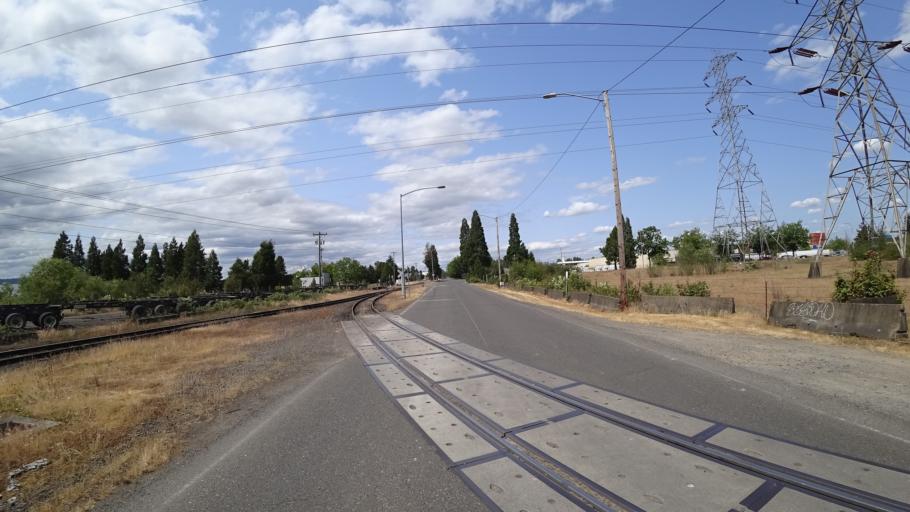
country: US
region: Oregon
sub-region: Washington County
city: Oak Hills
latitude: 45.6182
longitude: -122.7803
